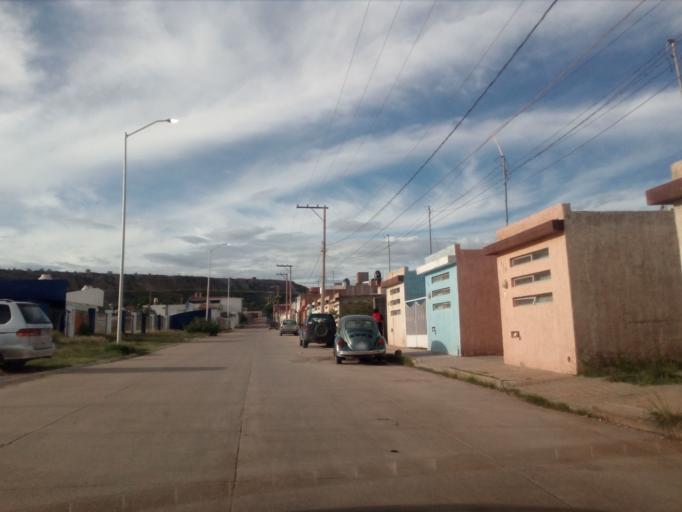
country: MX
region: Durango
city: Victoria de Durango
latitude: 24.0476
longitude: -104.6618
